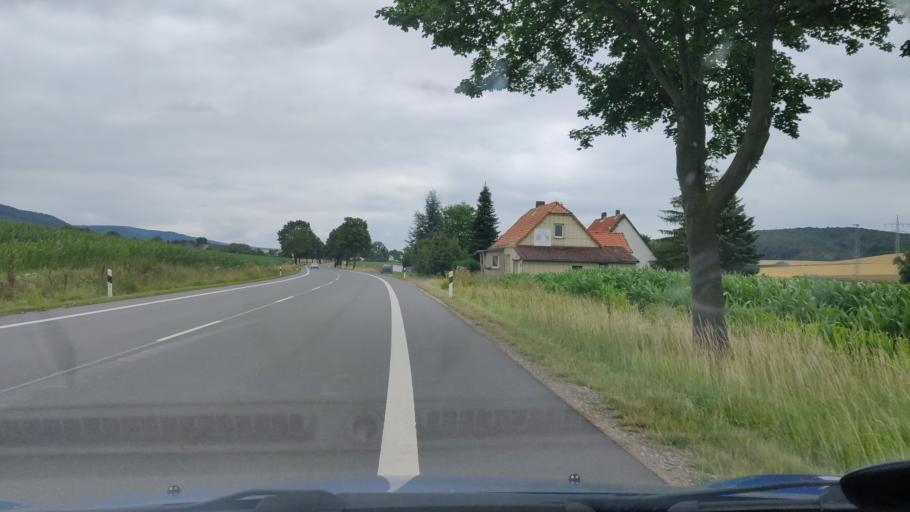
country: DE
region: Lower Saxony
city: Luerdissen
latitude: 51.9544
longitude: 9.6116
